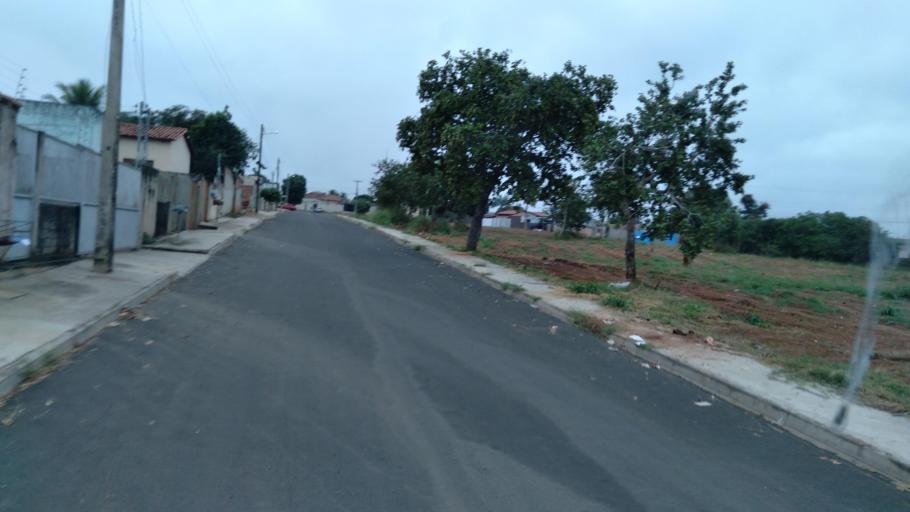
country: BR
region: Goias
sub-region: Mineiros
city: Mineiros
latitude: -17.5753
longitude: -52.5443
